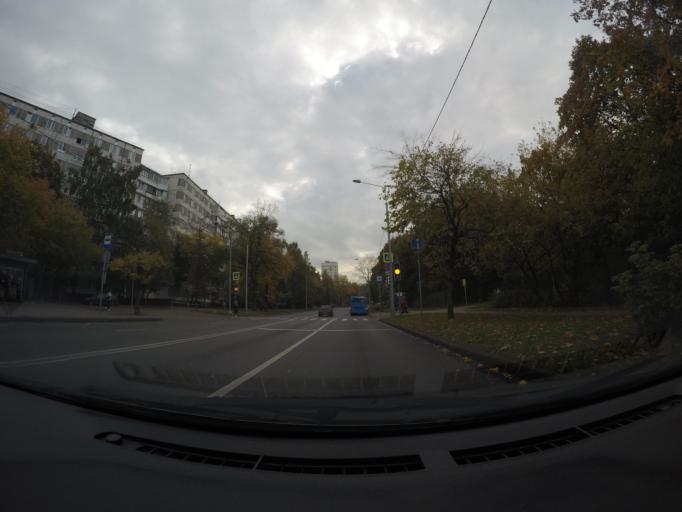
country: RU
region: Moscow
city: Ivanovskoye
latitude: 55.7649
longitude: 37.8224
